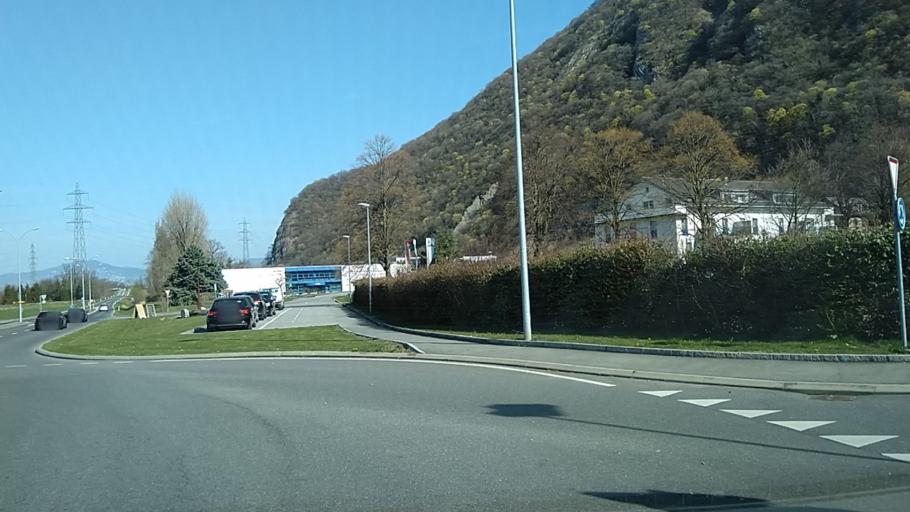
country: CH
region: Vaud
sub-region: Aigle District
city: Villeneuve
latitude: 46.3619
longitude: 6.9290
